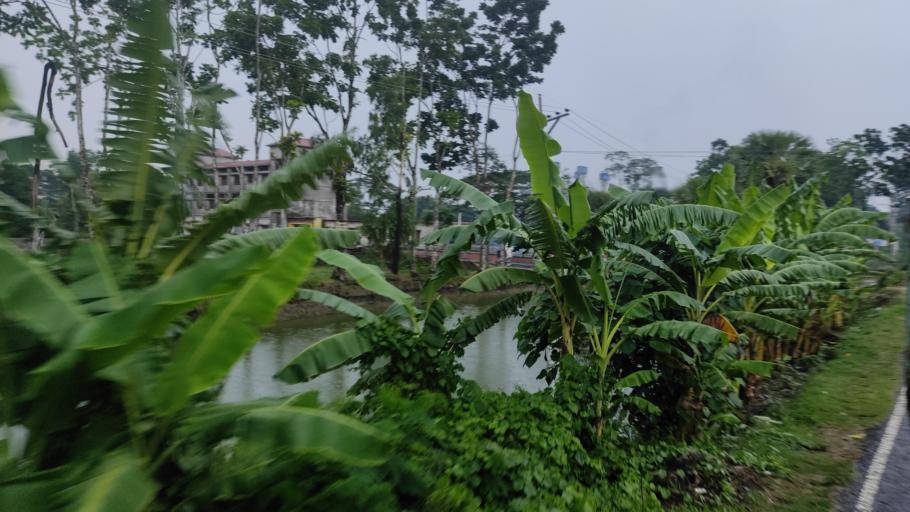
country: BD
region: Barisal
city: Bhandaria
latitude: 22.3109
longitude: 90.3250
